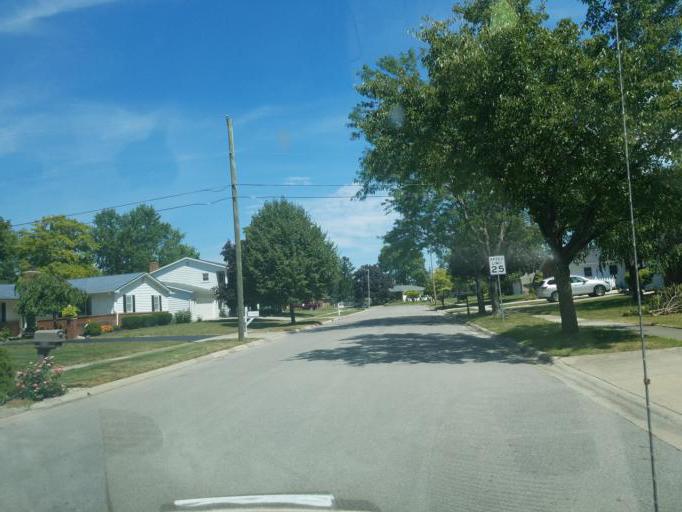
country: US
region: Ohio
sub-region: Franklin County
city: Grove City
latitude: 39.8726
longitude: -83.0753
